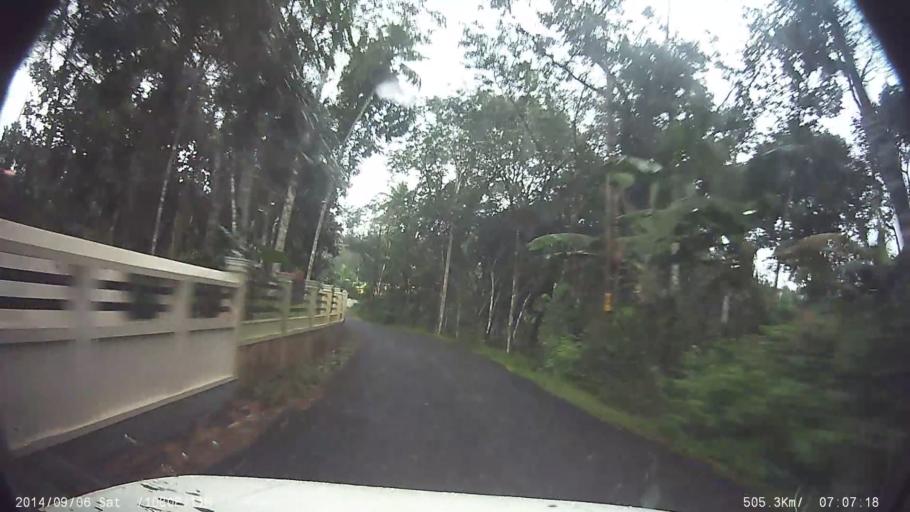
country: IN
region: Kerala
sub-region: Ernakulam
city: Piravam
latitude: 9.7947
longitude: 76.5369
